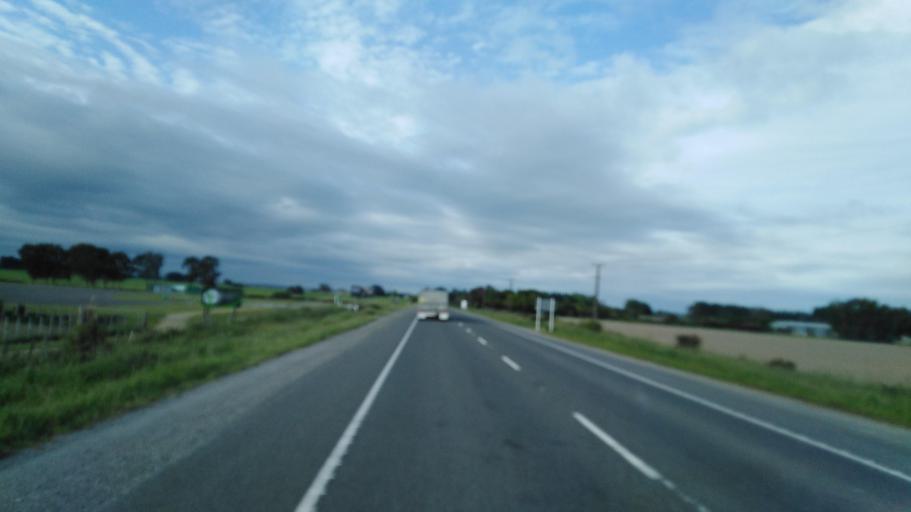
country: NZ
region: Manawatu-Wanganui
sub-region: Rangitikei District
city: Bulls
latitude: -40.2234
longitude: 175.4212
